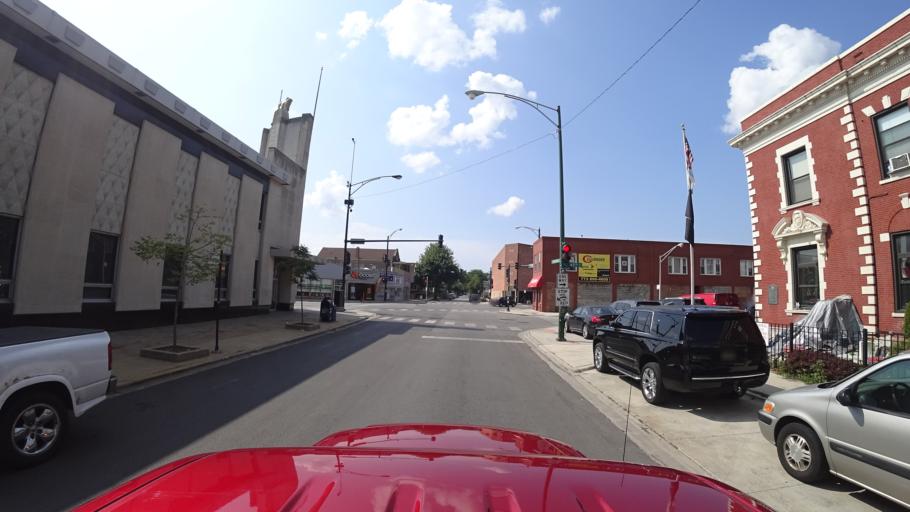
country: US
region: Illinois
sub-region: Cook County
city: Chicago
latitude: 41.8176
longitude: -87.6994
